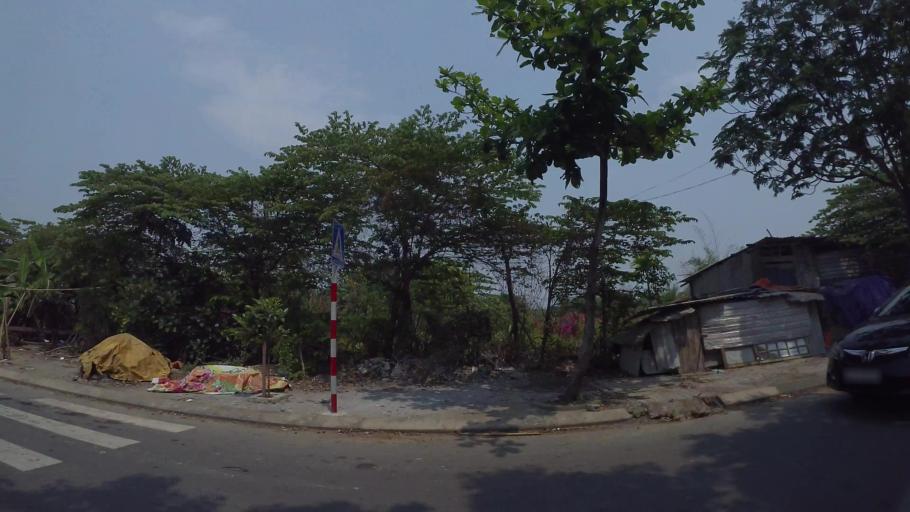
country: VN
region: Da Nang
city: Cam Le
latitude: 16.0065
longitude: 108.2120
